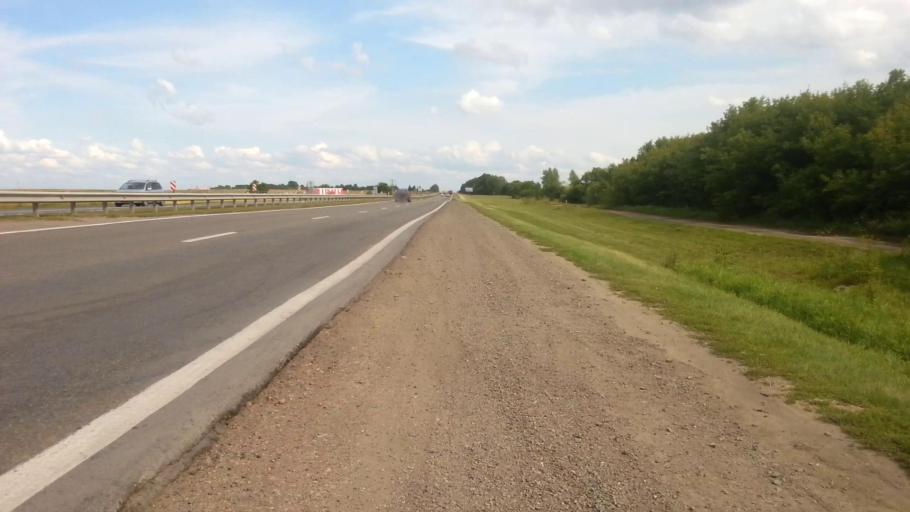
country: RU
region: Altai Krai
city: Nauchnyy Gorodok
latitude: 53.3565
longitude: 83.5082
